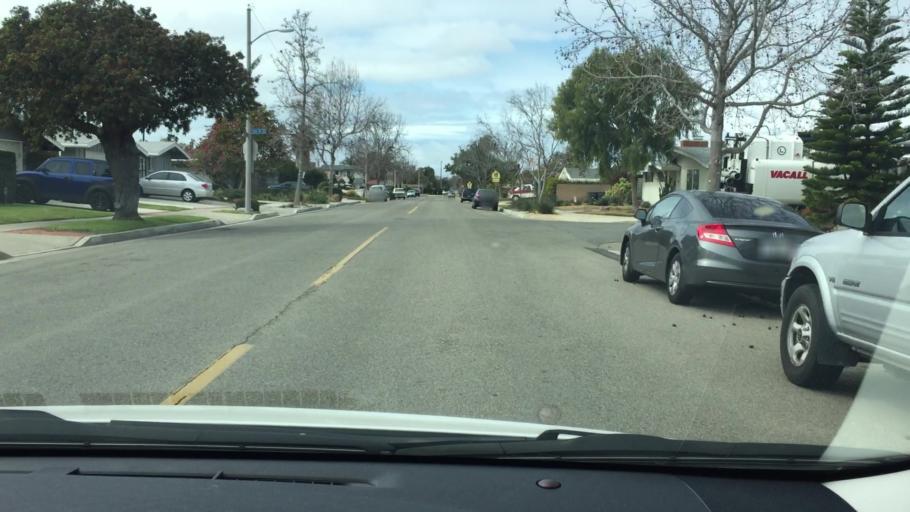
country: US
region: California
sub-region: Orange County
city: Costa Mesa
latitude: 33.6653
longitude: -117.9098
